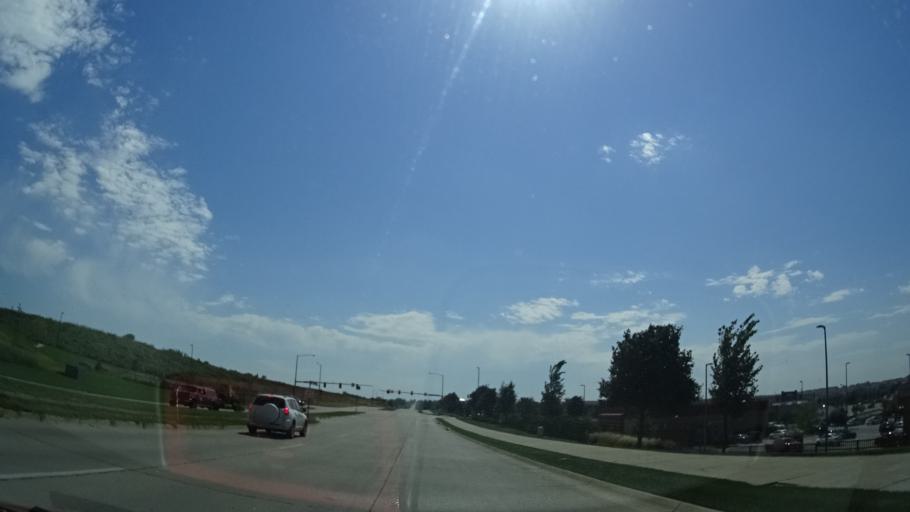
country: US
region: Nebraska
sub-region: Sarpy County
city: Papillion
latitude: 41.1362
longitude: -96.0238
